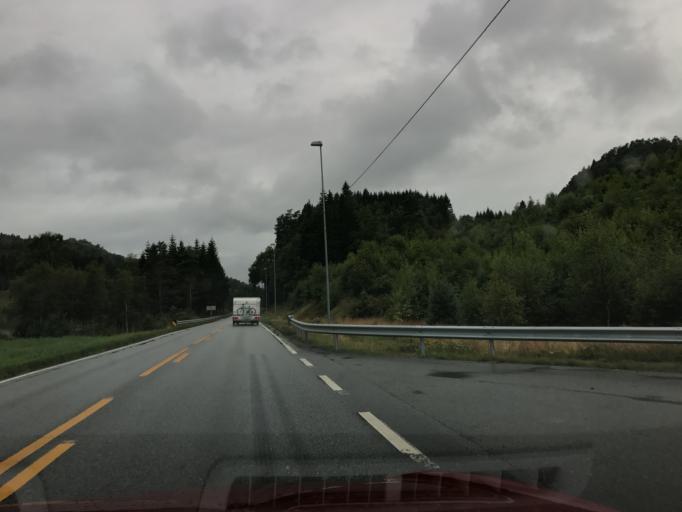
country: NO
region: Vest-Agder
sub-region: Lyngdal
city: Lyngdal
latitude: 58.1501
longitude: 7.1529
